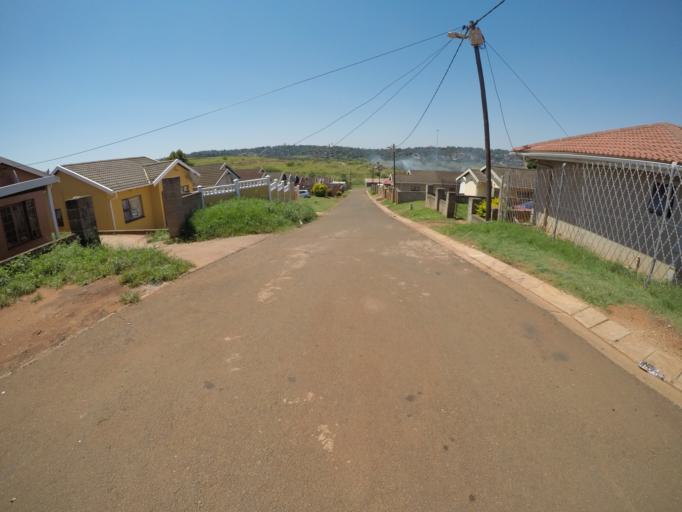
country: ZA
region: KwaZulu-Natal
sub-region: uThungulu District Municipality
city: Empangeni
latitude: -28.7719
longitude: 31.8813
